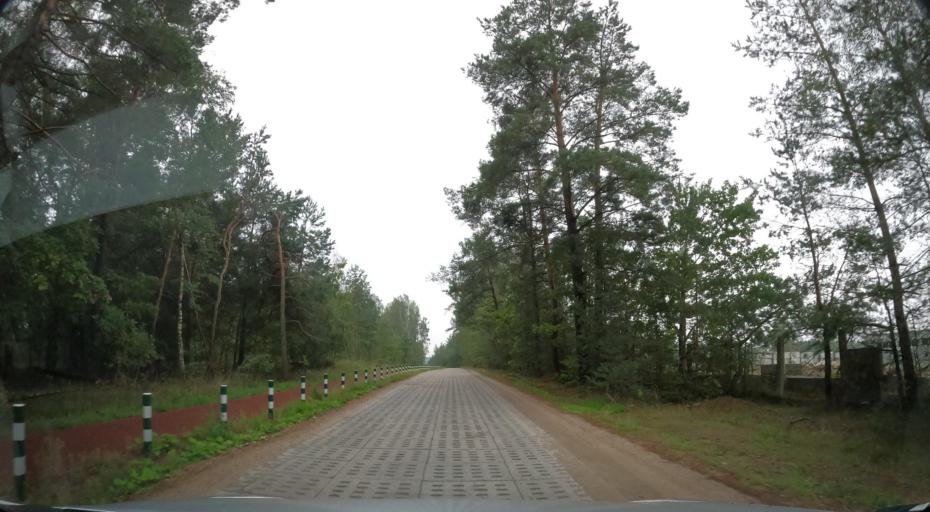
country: PL
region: Pomeranian Voivodeship
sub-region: Powiat kartuski
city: Chwaszczyno
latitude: 54.4252
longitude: 18.4153
